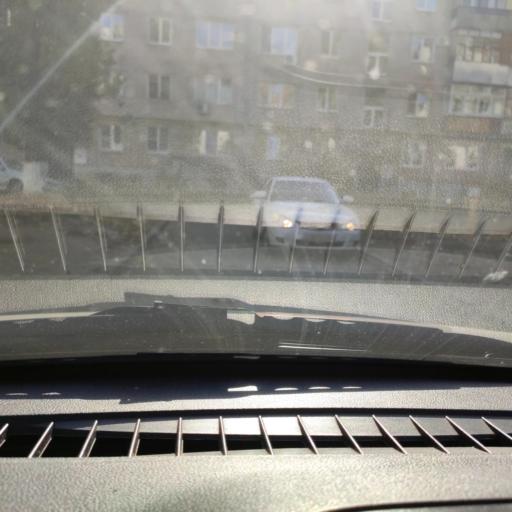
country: RU
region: Samara
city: Zhigulevsk
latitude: 53.4836
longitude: 49.4852
